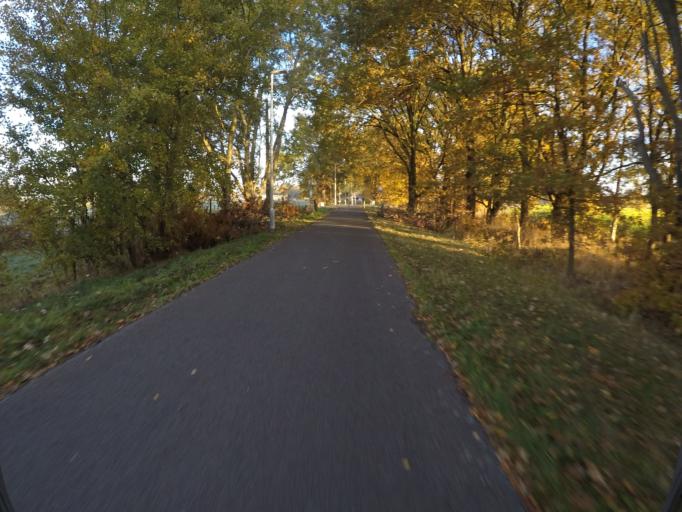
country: BE
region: Flanders
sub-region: Provincie Antwerpen
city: Olen
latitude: 51.1116
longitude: 4.8255
